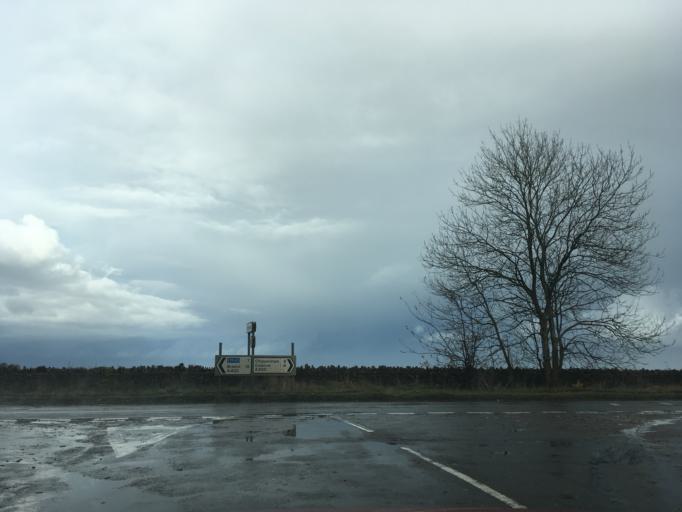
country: GB
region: England
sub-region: South Gloucestershire
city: Marshfield
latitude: 51.4632
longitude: -2.3101
